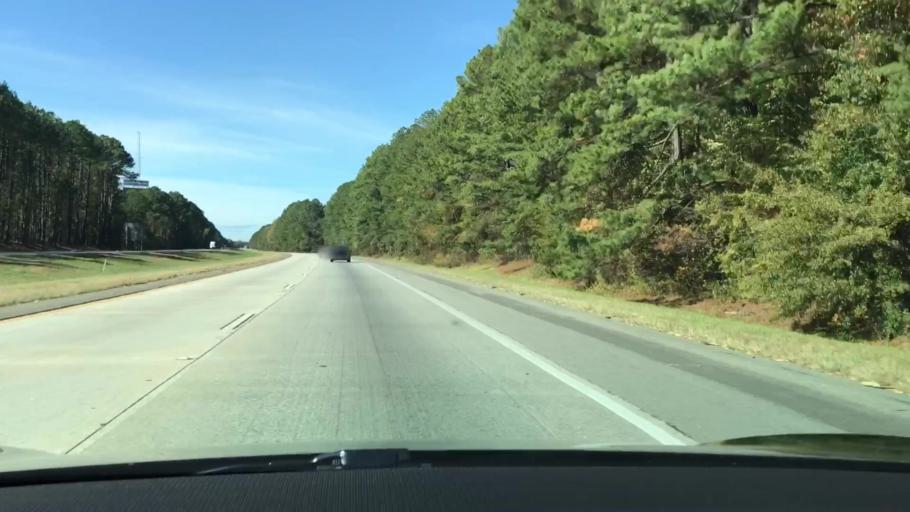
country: US
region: Georgia
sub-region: Taliaferro County
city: Crawfordville
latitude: 33.5306
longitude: -82.9293
